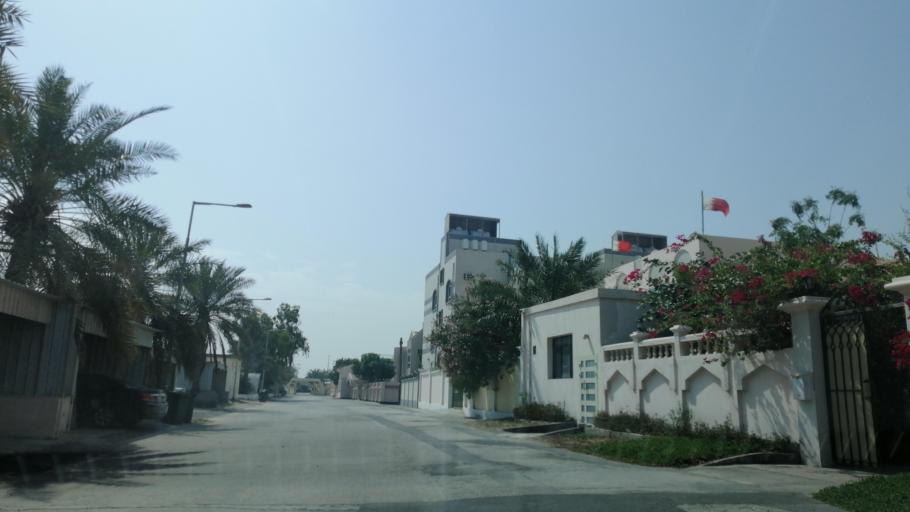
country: BH
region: Muharraq
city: Al Hadd
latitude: 26.2492
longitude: 50.6572
